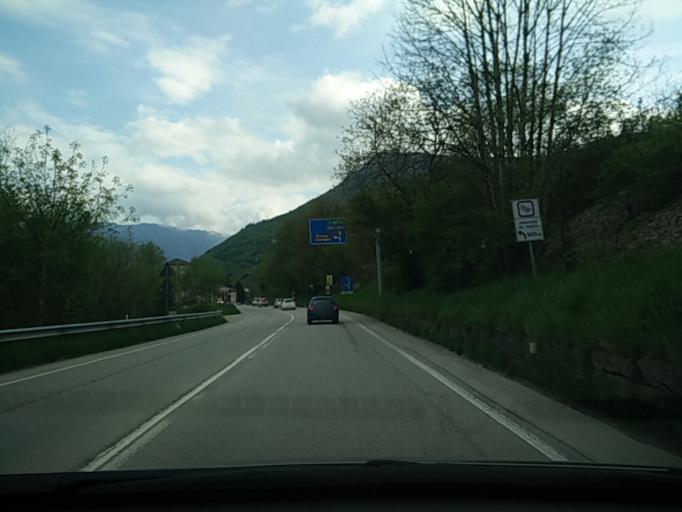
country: IT
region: Veneto
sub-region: Provincia di Belluno
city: Farra d'Alpago
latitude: 46.1349
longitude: 12.3167
